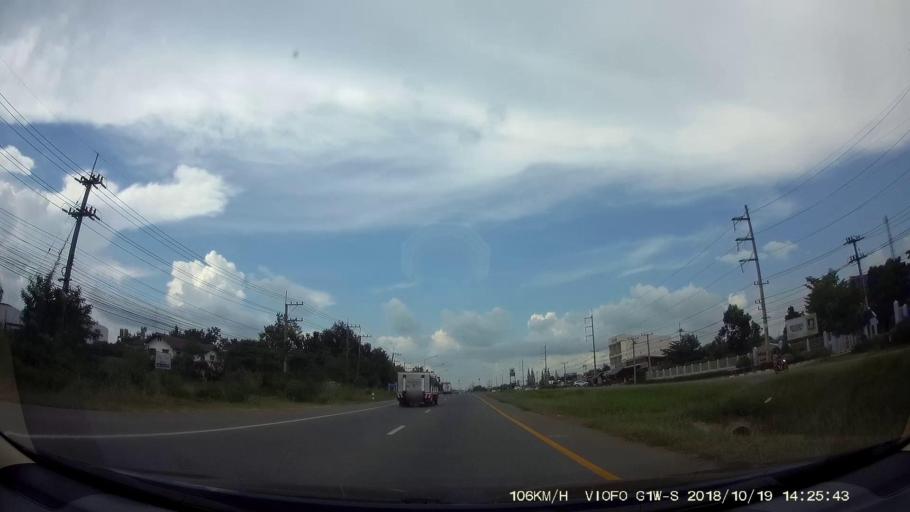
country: TH
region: Chaiyaphum
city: Kaeng Khro
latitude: 16.0976
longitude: 102.2630
